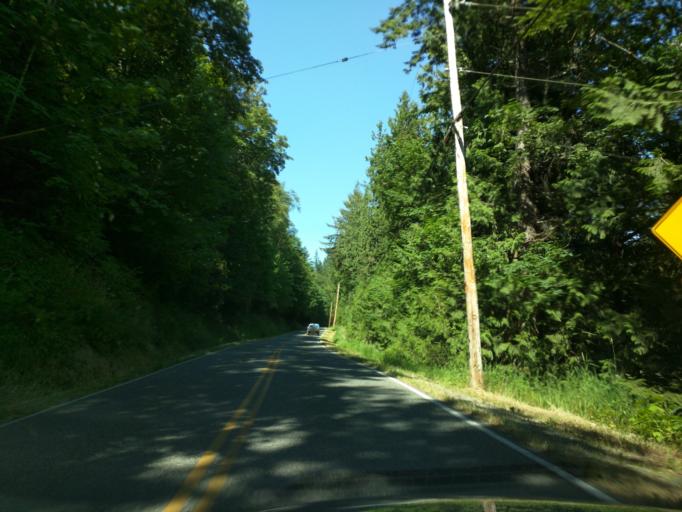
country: US
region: Washington
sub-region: Whatcom County
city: Sumas
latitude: 48.9393
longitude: -122.2430
